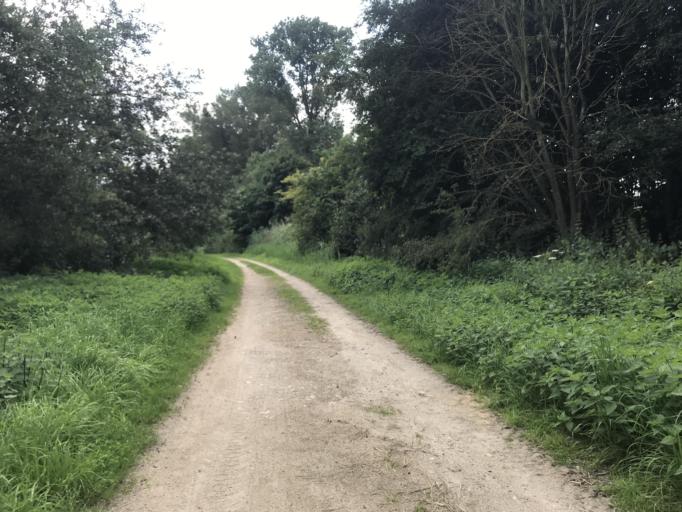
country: DE
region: Hesse
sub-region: Regierungsbezirk Darmstadt
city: Bischofsheim
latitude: 50.0157
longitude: 8.3850
